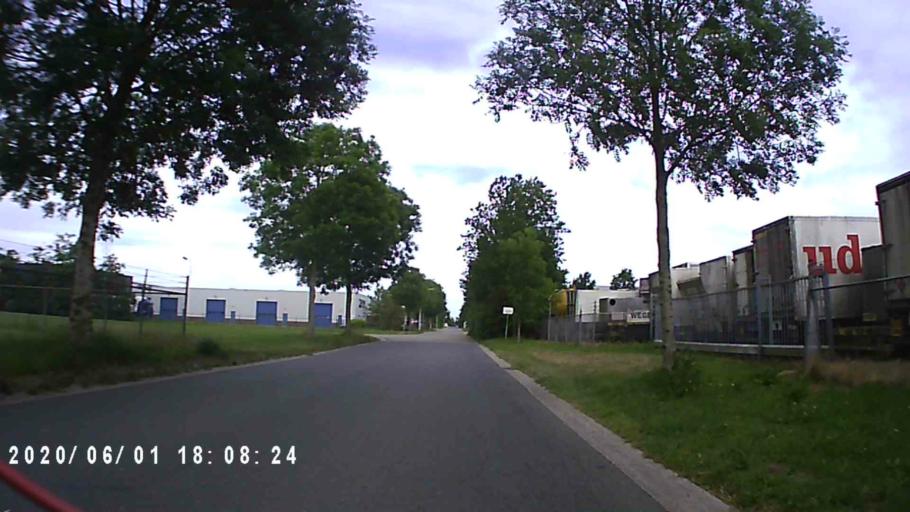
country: NL
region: Friesland
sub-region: Gemeente Tytsjerksteradiel
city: Sumar
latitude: 53.1820
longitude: 6.0015
